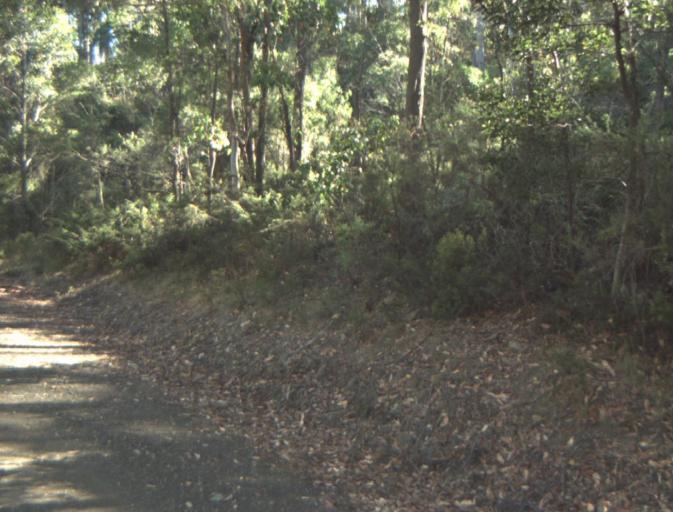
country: AU
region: Tasmania
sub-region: Launceston
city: Newstead
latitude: -41.3075
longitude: 147.3349
